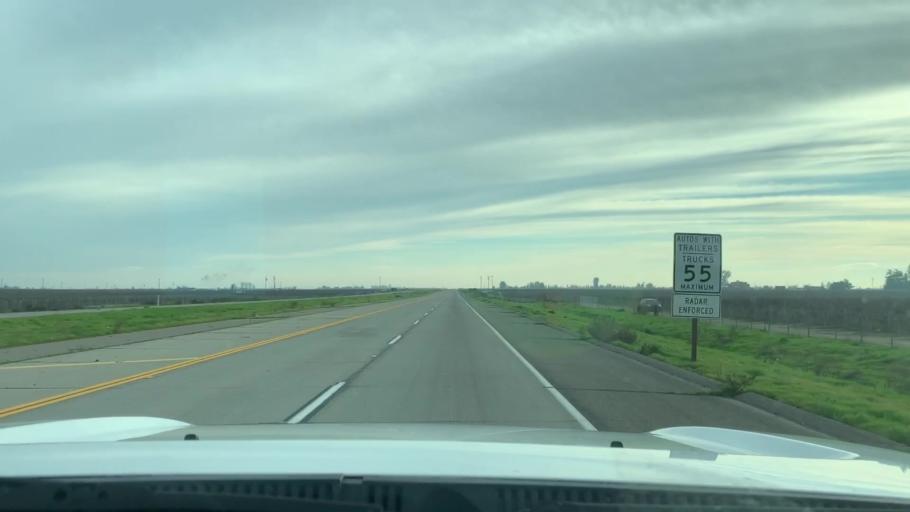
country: US
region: California
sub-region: Fresno County
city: Caruthers
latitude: 36.5743
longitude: -119.7863
